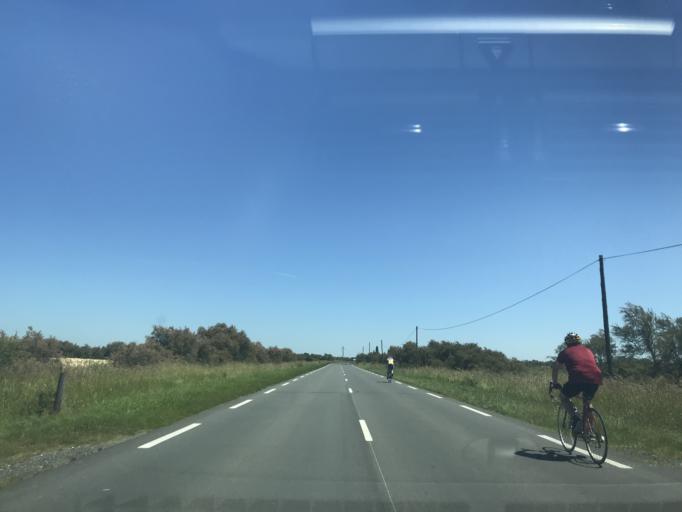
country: FR
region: Poitou-Charentes
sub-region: Departement de la Charente-Maritime
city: Meschers-sur-Gironde
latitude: 45.5602
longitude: -0.9313
